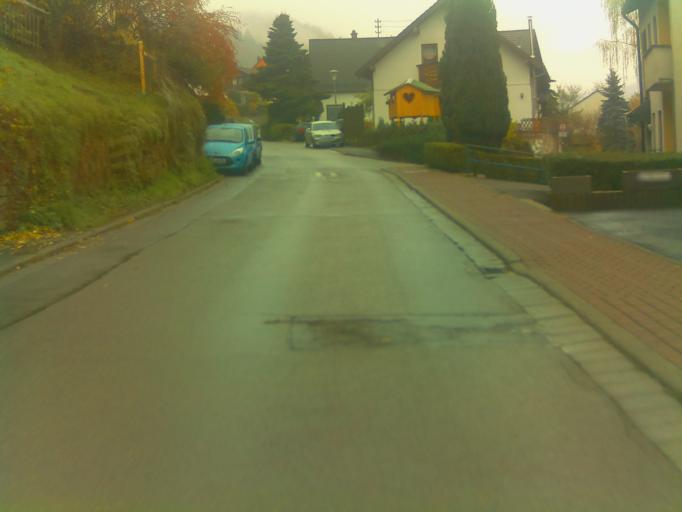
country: DE
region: Baden-Wuerttemberg
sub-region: Karlsruhe Region
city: Schonau
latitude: 49.4395
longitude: 8.8087
